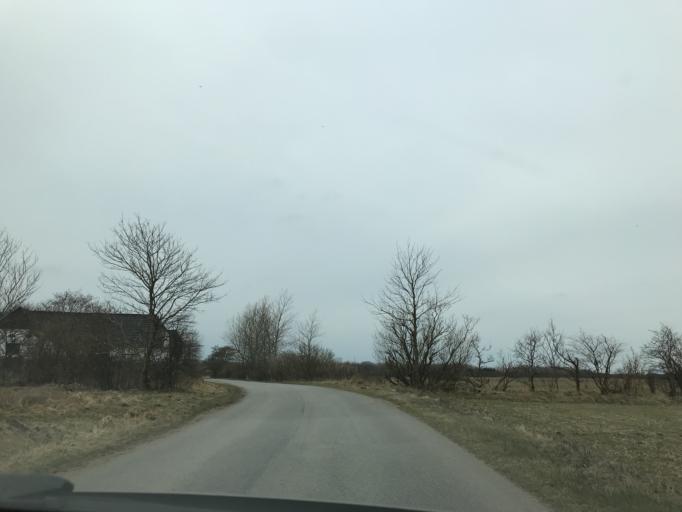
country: DK
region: South Denmark
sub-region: Varde Kommune
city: Oksbol
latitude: 55.8041
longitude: 8.3554
